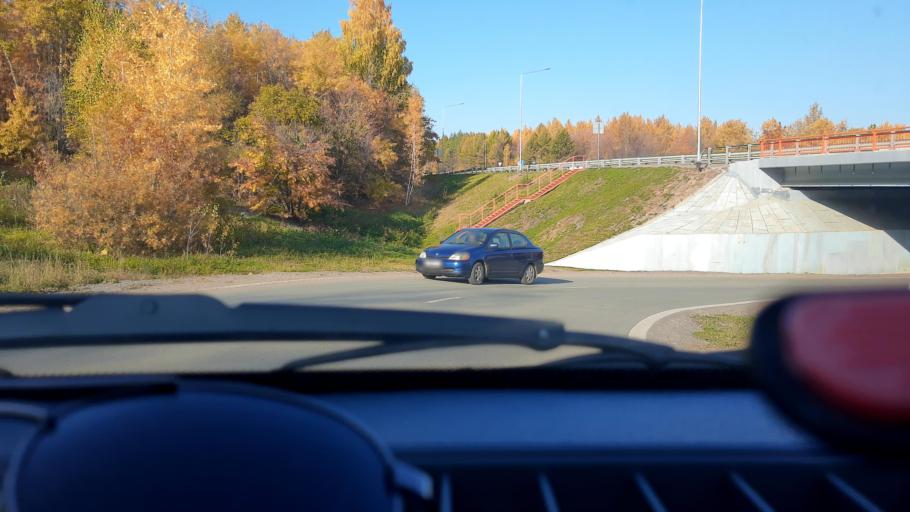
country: RU
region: Bashkortostan
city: Karmaskaly
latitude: 54.3798
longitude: 55.9165
